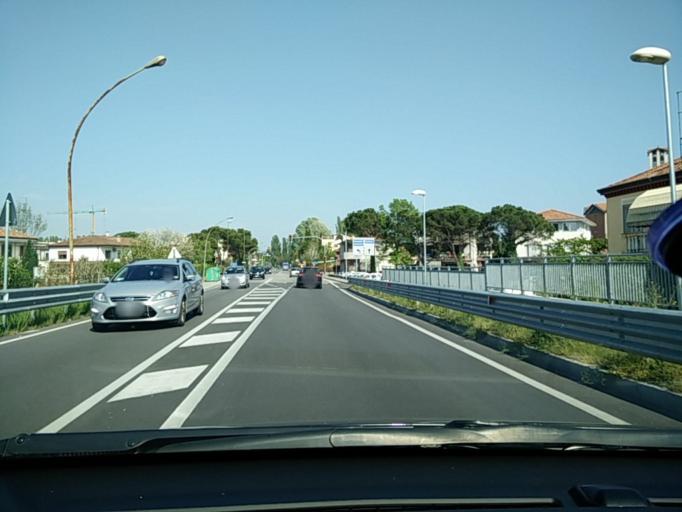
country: IT
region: Veneto
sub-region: Provincia di Venezia
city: Mira Taglio
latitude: 45.4398
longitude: 12.1382
